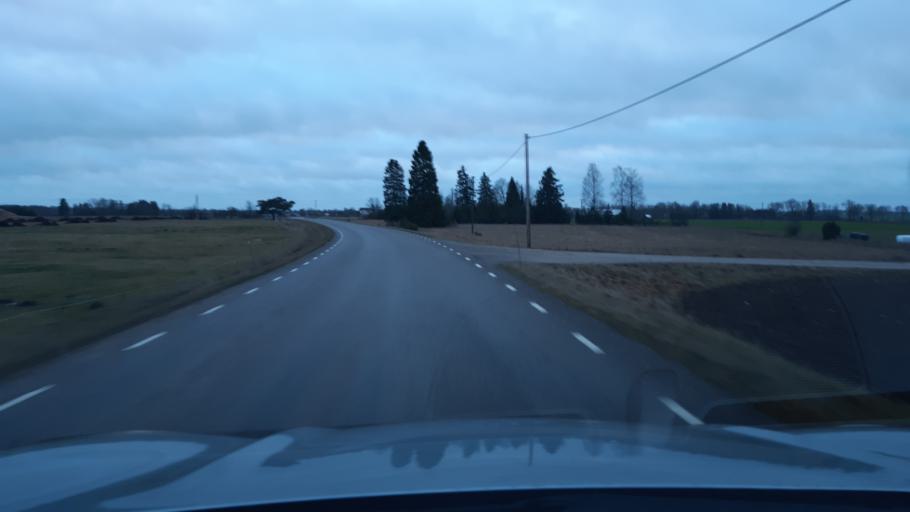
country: EE
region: Raplamaa
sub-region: Kohila vald
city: Kohila
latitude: 59.0680
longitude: 24.6837
